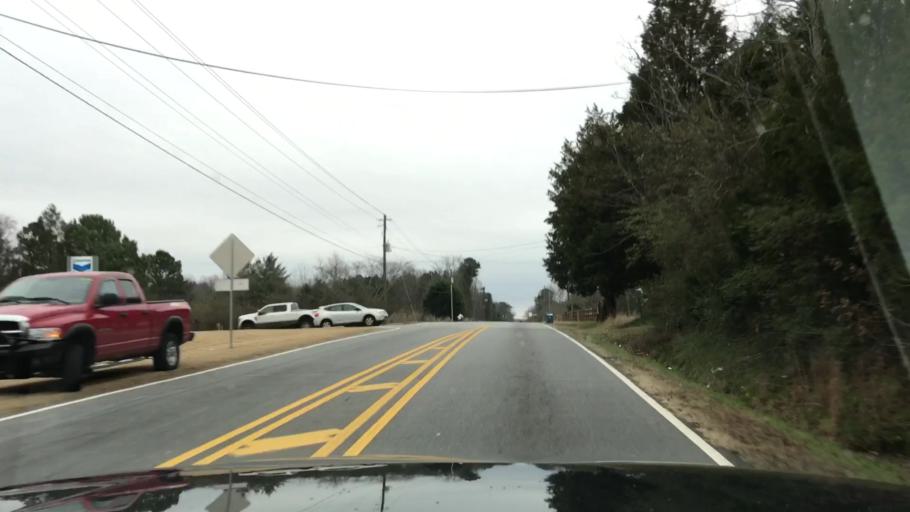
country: US
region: Georgia
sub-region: Gwinnett County
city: Dacula
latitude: 33.9712
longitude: -83.8898
